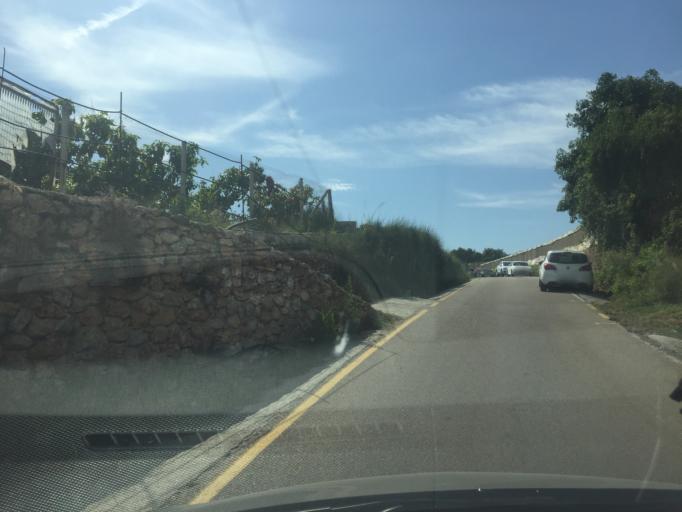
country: ES
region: Andalusia
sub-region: Provincia de Malaga
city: Nerja
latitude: 36.7554
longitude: -3.8377
